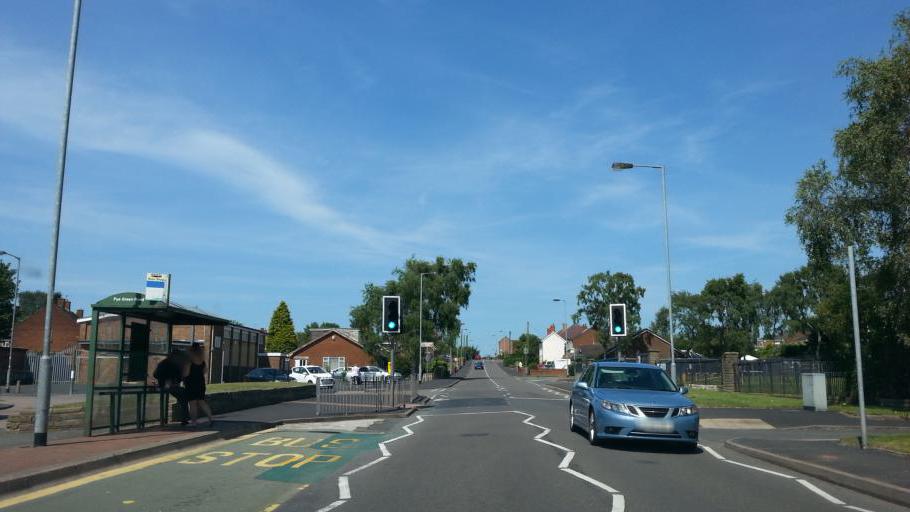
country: GB
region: England
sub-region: Staffordshire
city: Cannock
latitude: 52.7097
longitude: -2.0252
